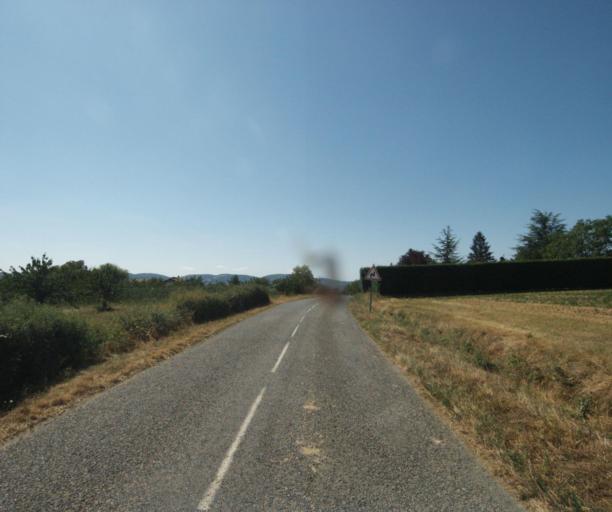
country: FR
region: Rhone-Alpes
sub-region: Departement du Rhone
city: Bessenay
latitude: 45.7973
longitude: 4.5558
